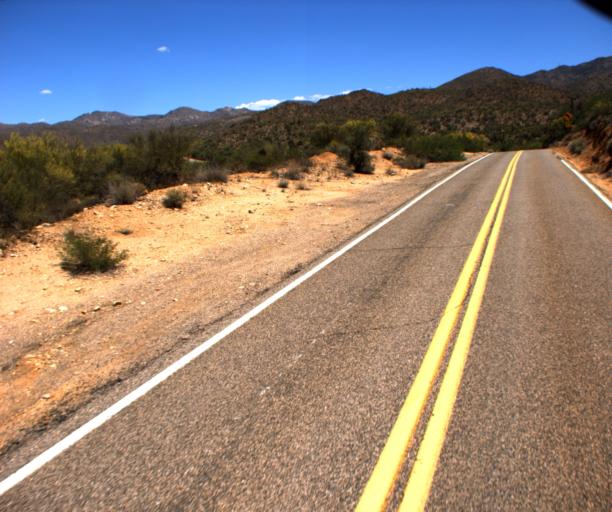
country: US
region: Arizona
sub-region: Yavapai County
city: Bagdad
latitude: 34.4598
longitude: -113.0375
